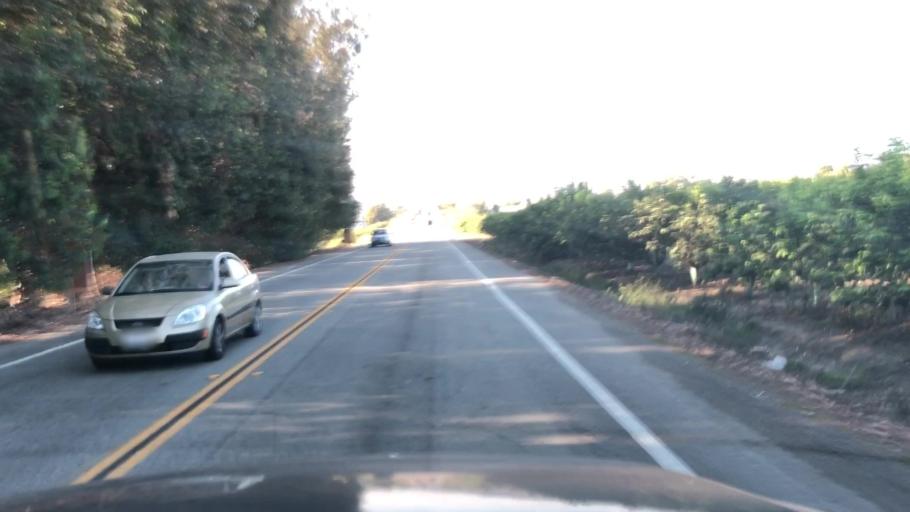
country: US
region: California
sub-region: Ventura County
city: Oxnard Shores
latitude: 34.2472
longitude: -119.2342
